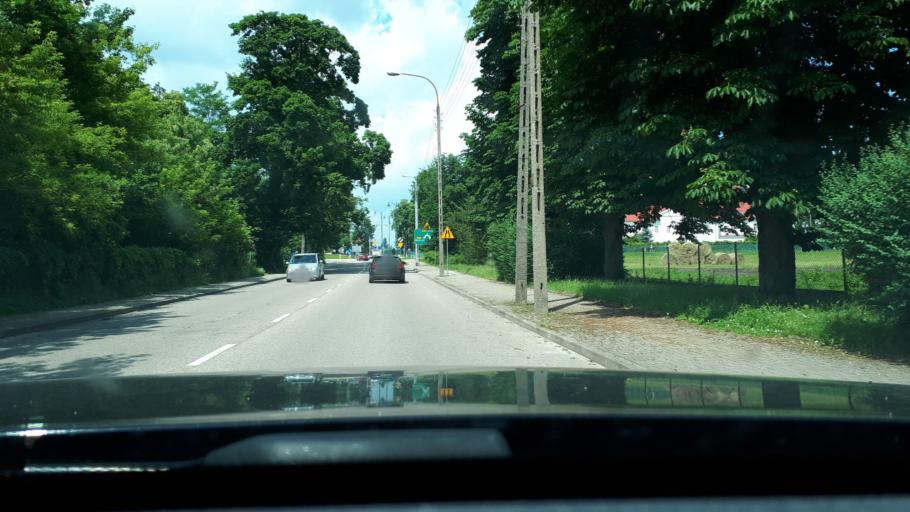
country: PL
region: Podlasie
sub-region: Powiat bialostocki
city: Suprasl
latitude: 53.2087
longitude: 23.3367
